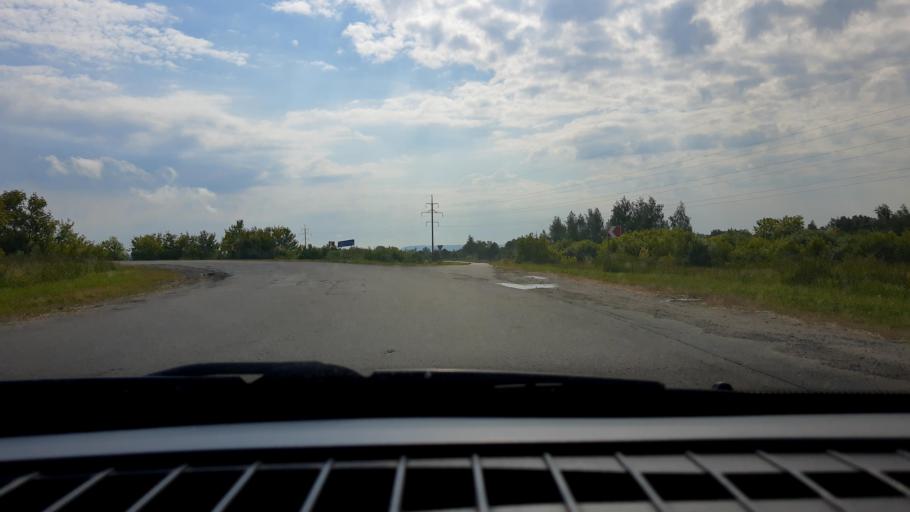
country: RU
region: Nizjnij Novgorod
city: Kstovo
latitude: 56.1097
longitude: 44.2870
